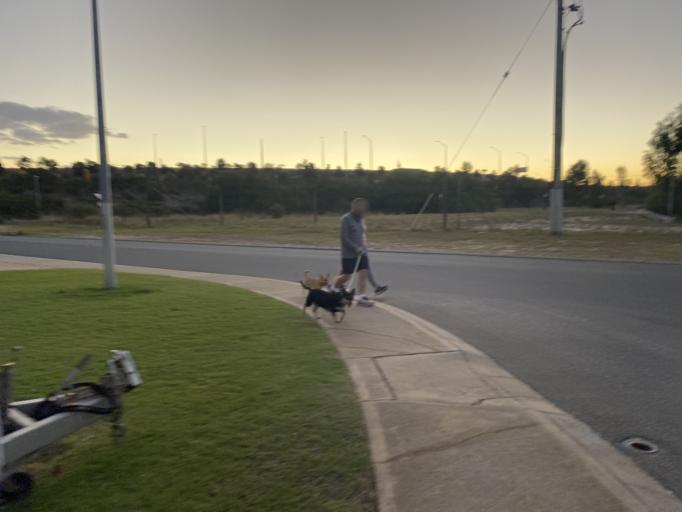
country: AU
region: Western Australia
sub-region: Belmont
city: Kewdale
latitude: -31.9870
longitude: 115.9897
